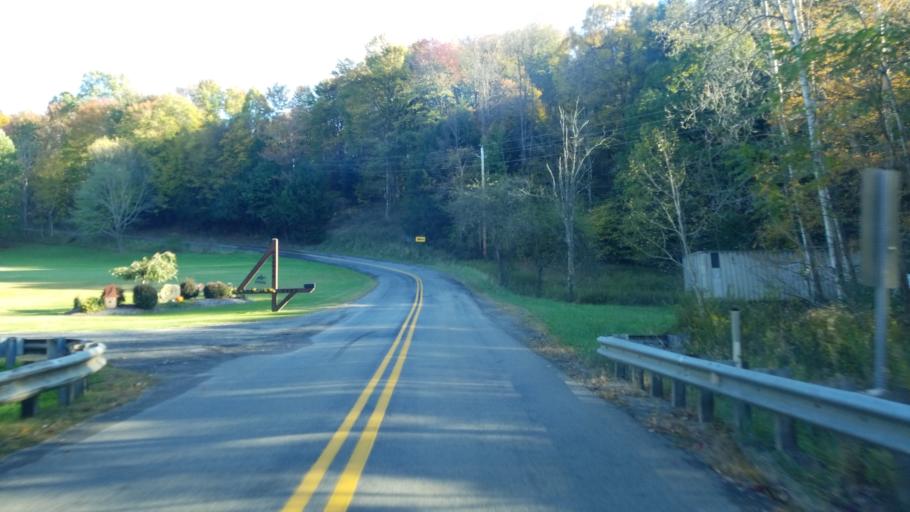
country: US
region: Pennsylvania
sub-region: Indiana County
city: Johnsonburg
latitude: 40.9135
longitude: -78.8811
